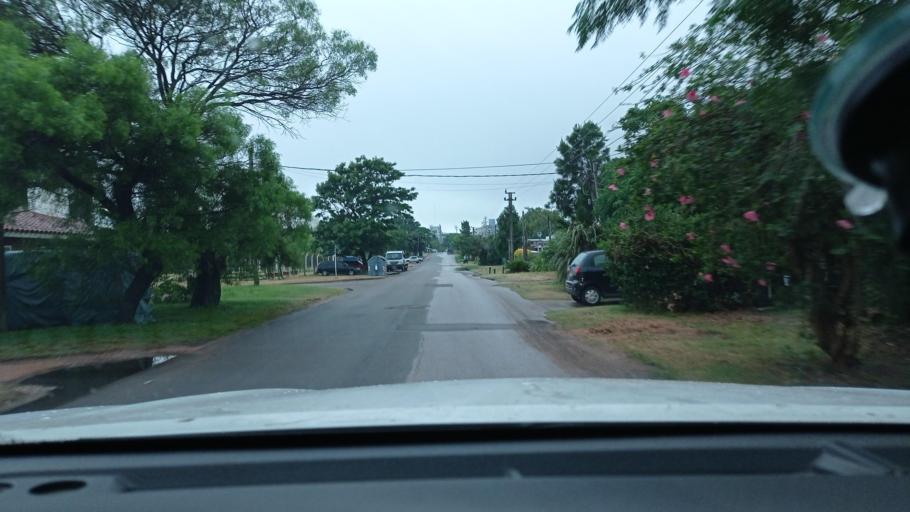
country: UY
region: Maldonado
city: Maldonado
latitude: -34.9148
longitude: -54.9657
